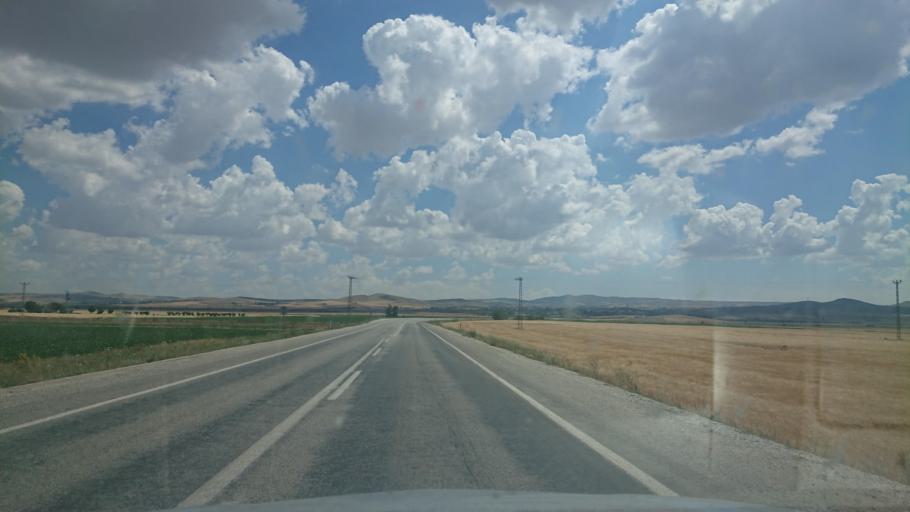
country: TR
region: Aksaray
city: Sariyahsi
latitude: 39.0157
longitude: 33.8675
